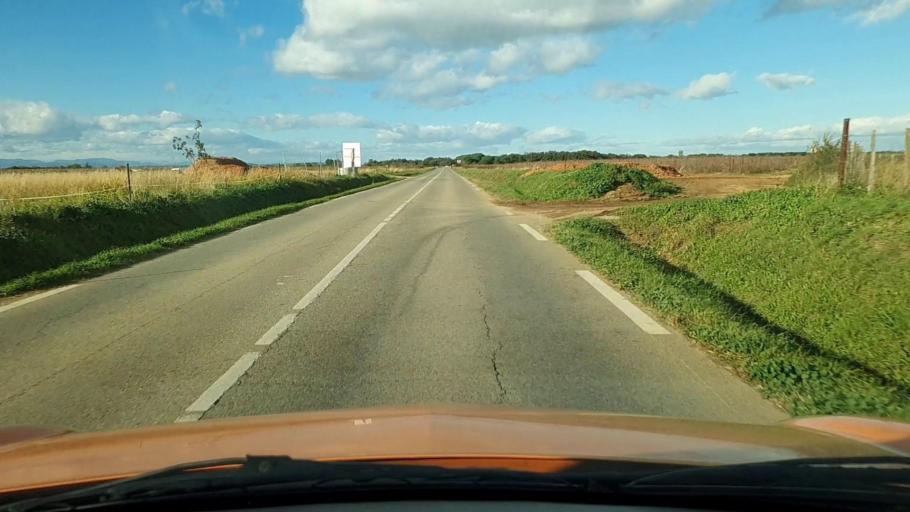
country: FR
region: Languedoc-Roussillon
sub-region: Departement du Gard
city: Vauvert
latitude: 43.6753
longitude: 4.2802
